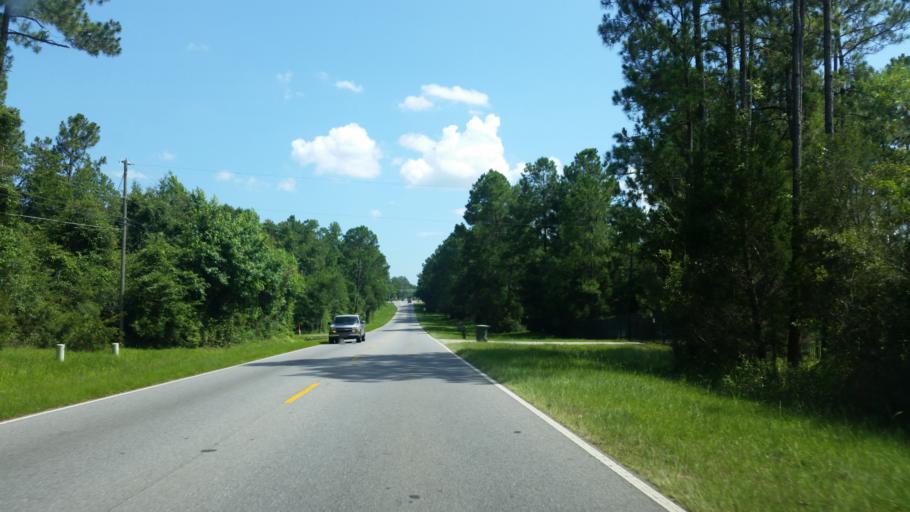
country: US
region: Florida
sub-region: Escambia County
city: Cantonment
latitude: 30.5401
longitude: -87.3805
